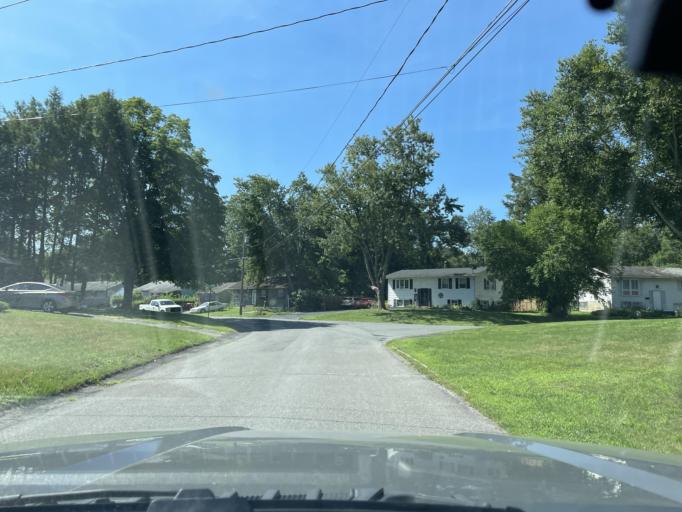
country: US
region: New York
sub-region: Ulster County
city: Saugerties South
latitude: 42.0648
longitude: -73.9575
